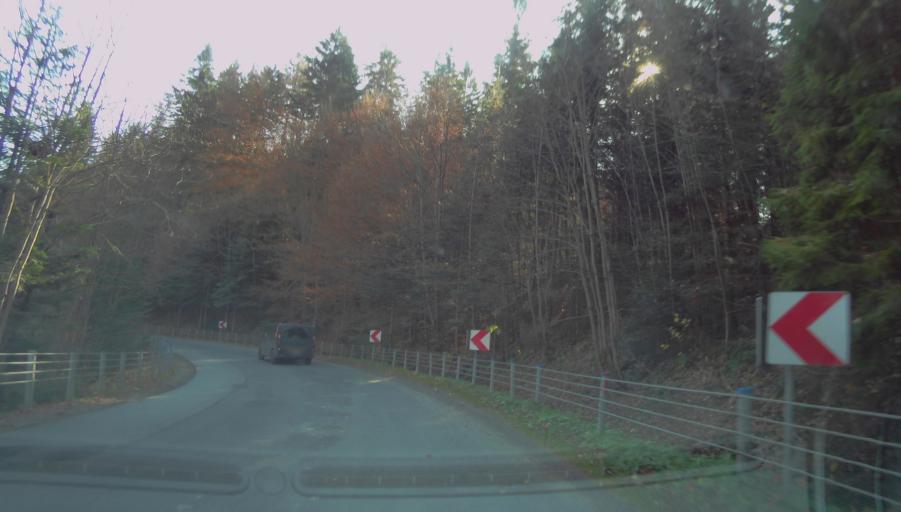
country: PL
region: Subcarpathian Voivodeship
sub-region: Powiat leski
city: Cisna
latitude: 49.2045
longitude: 22.2989
